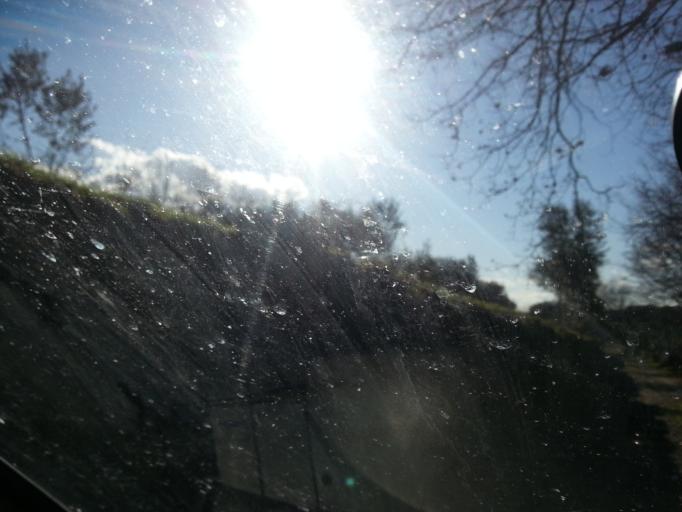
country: PT
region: Guarda
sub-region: Fornos de Algodres
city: Fornos de Algodres
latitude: 40.6113
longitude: -7.5015
